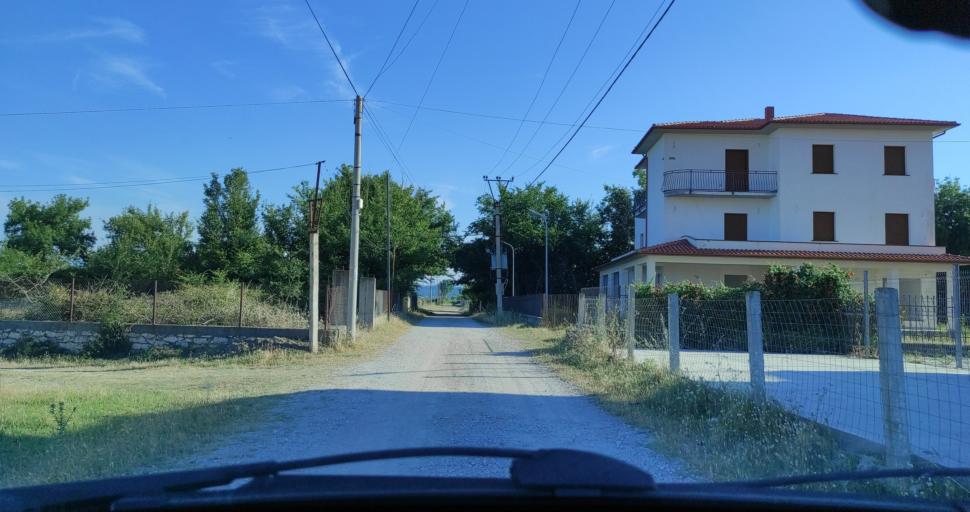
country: AL
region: Shkoder
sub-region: Rrethi i Shkodres
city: Velipoje
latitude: 41.8688
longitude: 19.4261
